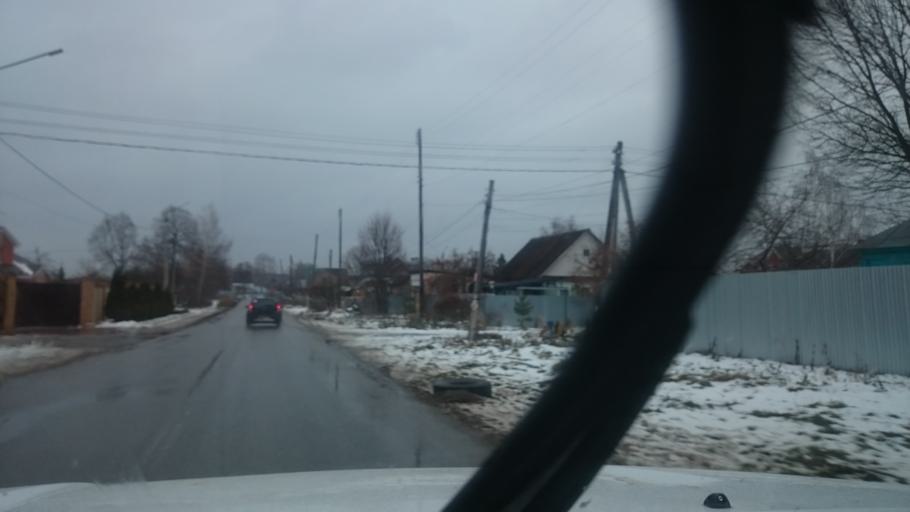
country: RU
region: Tula
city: Tula
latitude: 54.2052
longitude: 37.5621
